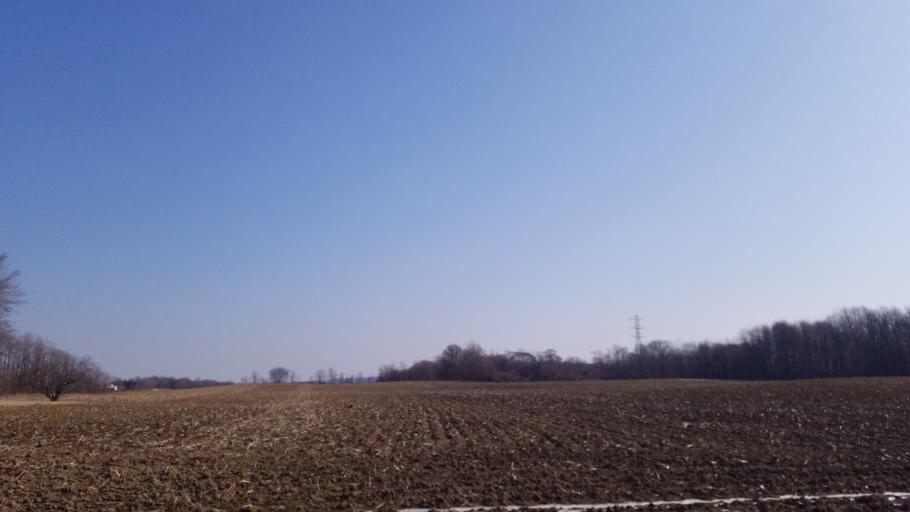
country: US
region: Ohio
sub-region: Richland County
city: Ontario
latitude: 40.8550
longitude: -82.5521
